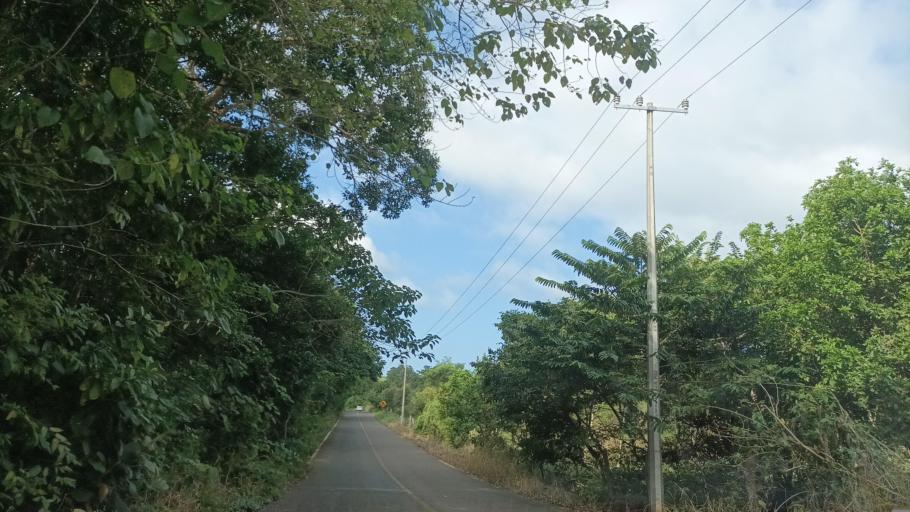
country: MX
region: Veracruz
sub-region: Pajapan
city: Pajapan
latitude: 18.1861
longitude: -94.6791
